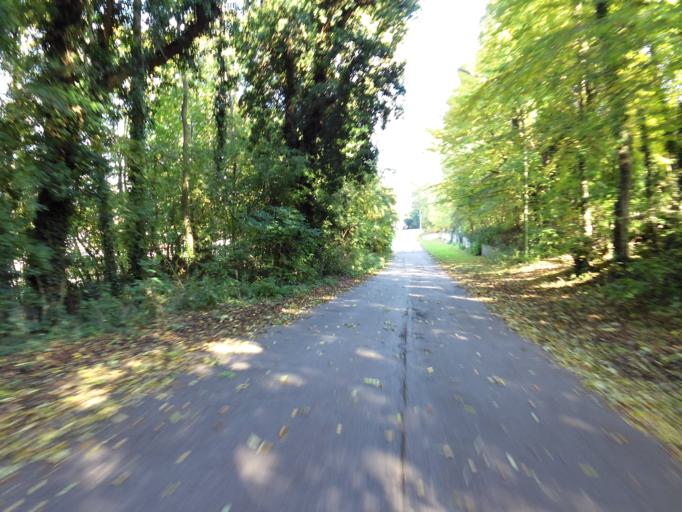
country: DE
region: North Rhine-Westphalia
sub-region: Regierungsbezirk Koln
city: Ubach-Palenberg
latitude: 50.9139
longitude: 6.1136
